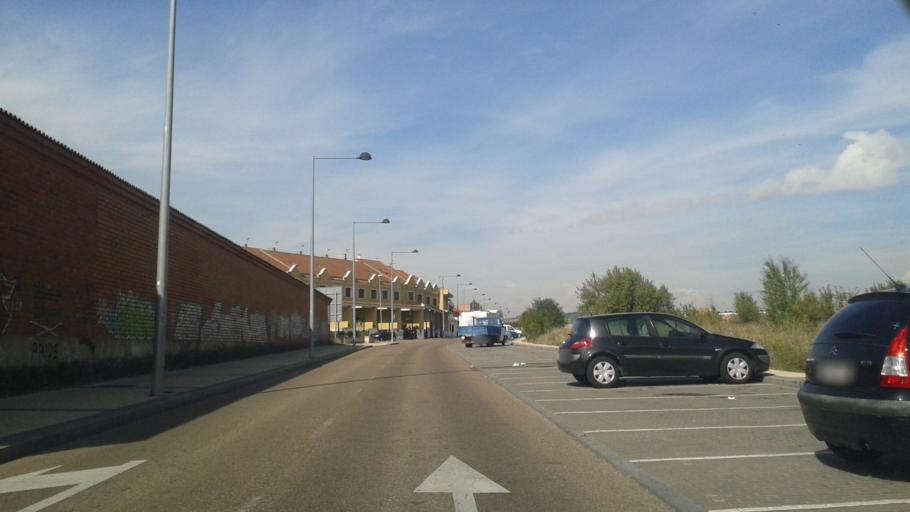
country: ES
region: Castille and Leon
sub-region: Provincia de Valladolid
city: Arroyo
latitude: 41.6288
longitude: -4.7706
